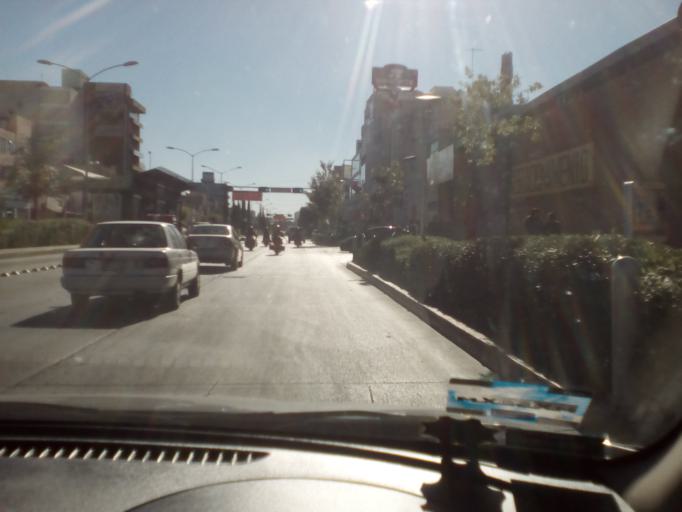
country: MX
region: Guanajuato
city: Leon
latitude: 21.1248
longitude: -101.6807
